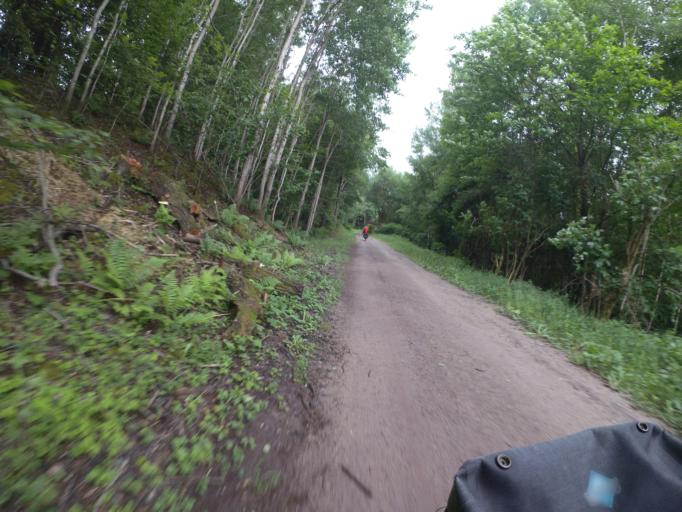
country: DE
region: Rheinland-Pfalz
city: Obersimten
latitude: 49.1709
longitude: 7.5994
